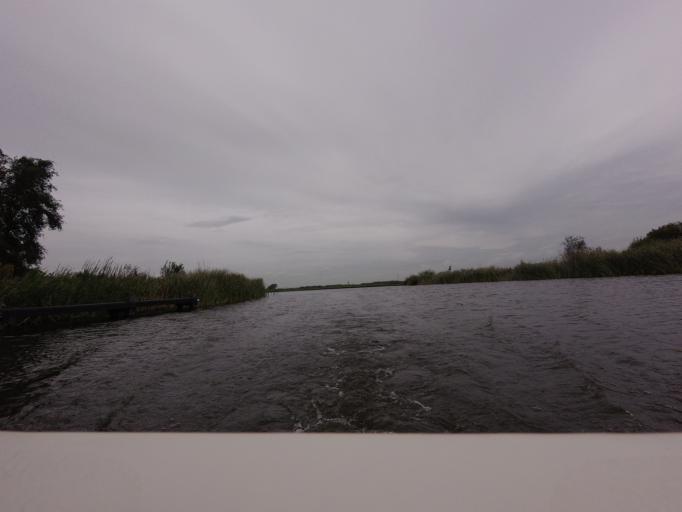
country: NL
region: Friesland
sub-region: Gemeente Boarnsterhim
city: Warten
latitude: 53.1134
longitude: 5.8881
